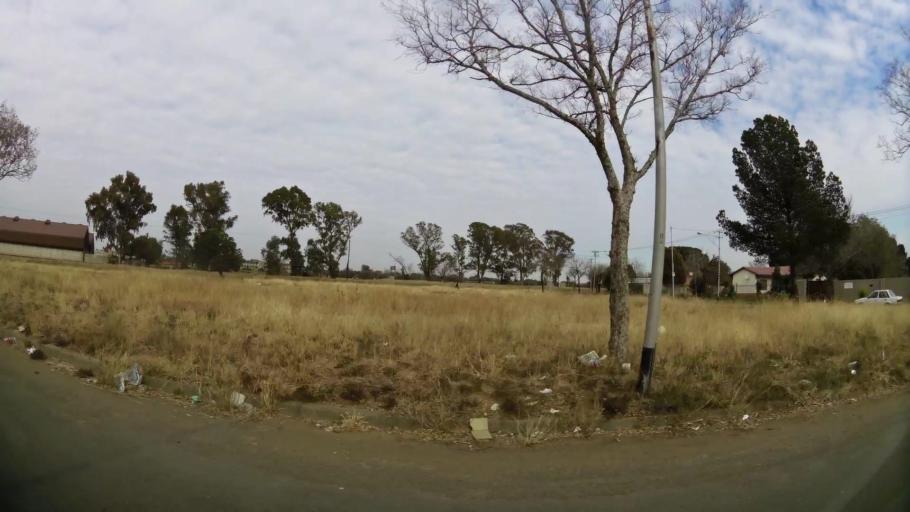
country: ZA
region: Orange Free State
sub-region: Mangaung Metropolitan Municipality
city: Bloemfontein
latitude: -29.1323
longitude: 26.2026
